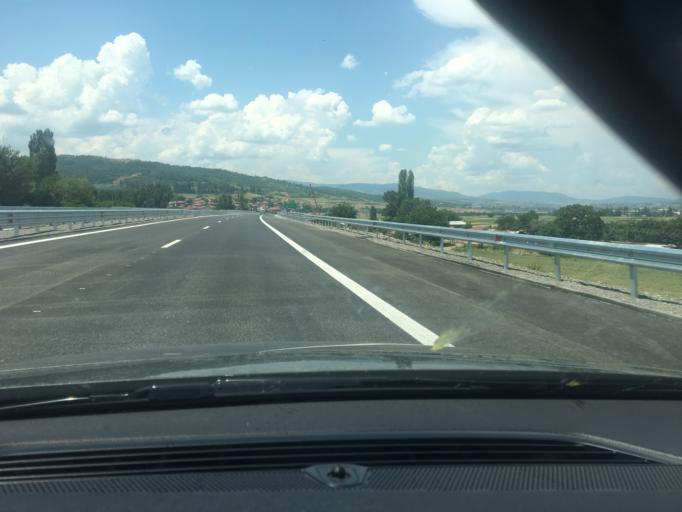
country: BG
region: Blagoevgrad
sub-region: Obshtina Blagoevgrad
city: Blagoevgrad
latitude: 41.9796
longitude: 23.0651
